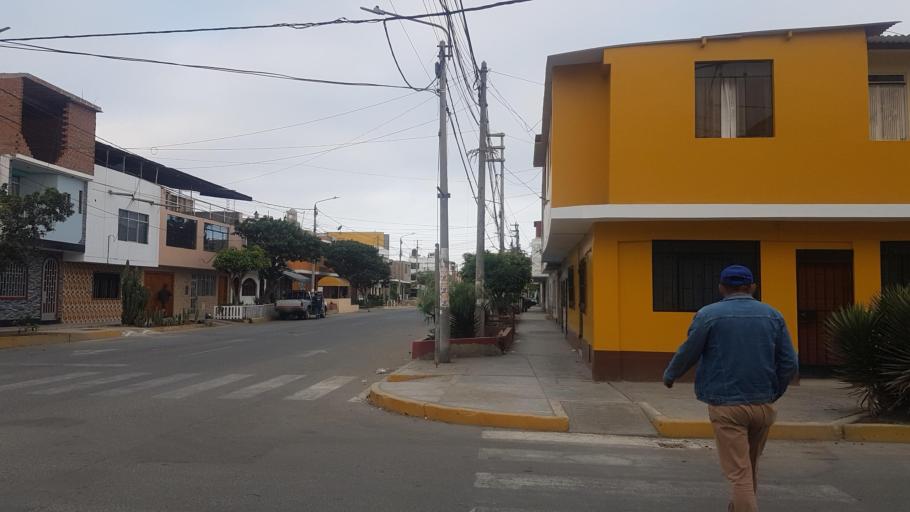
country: PE
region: Ancash
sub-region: Provincia de Santa
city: Chimbote
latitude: -9.0933
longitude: -78.5716
